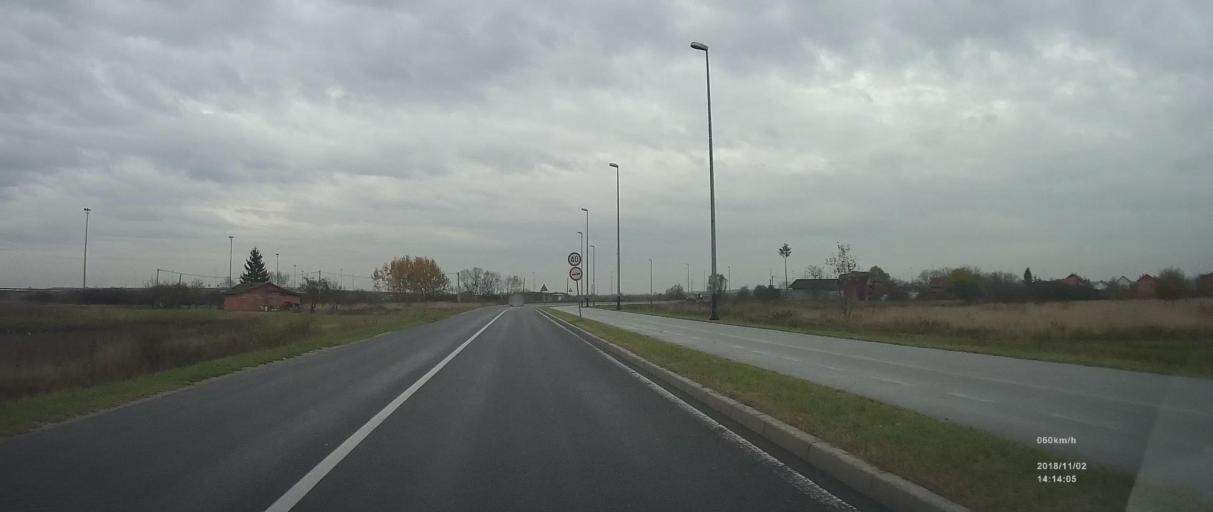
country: HR
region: Zagrebacka
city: Gradici
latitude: 45.6939
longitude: 16.0607
